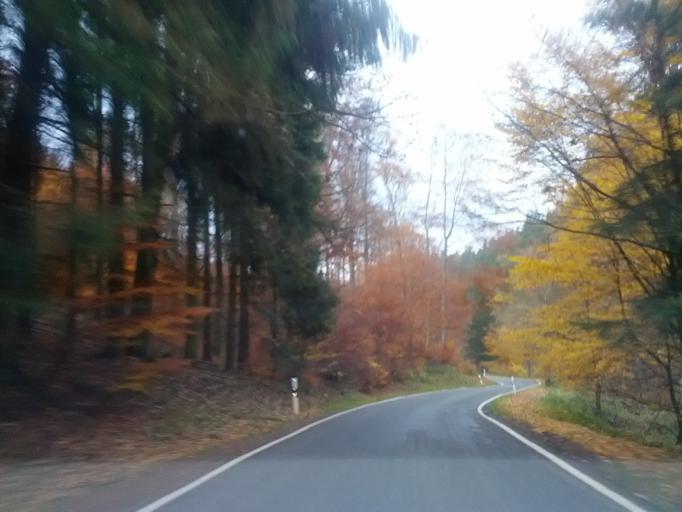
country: DE
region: Thuringia
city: Ruhla
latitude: 50.8925
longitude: 10.3239
